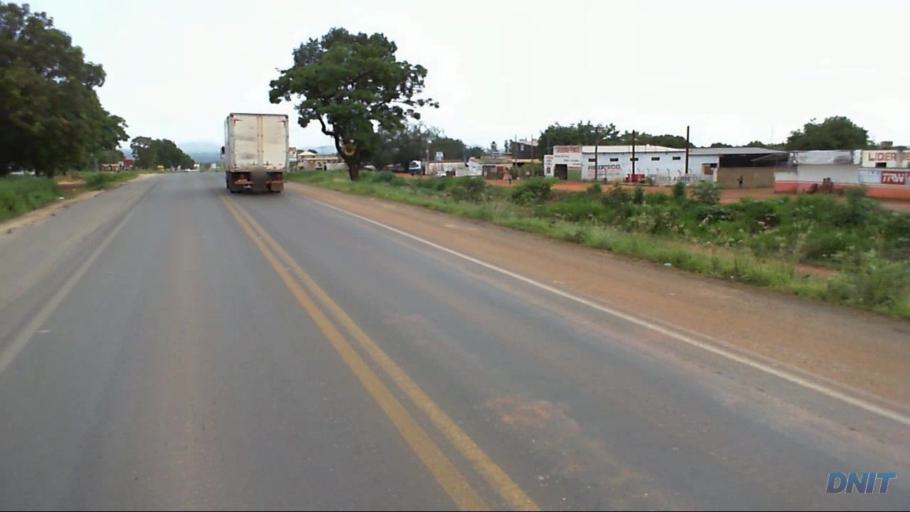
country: BR
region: Goias
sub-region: Uruacu
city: Uruacu
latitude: -14.5455
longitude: -49.1611
